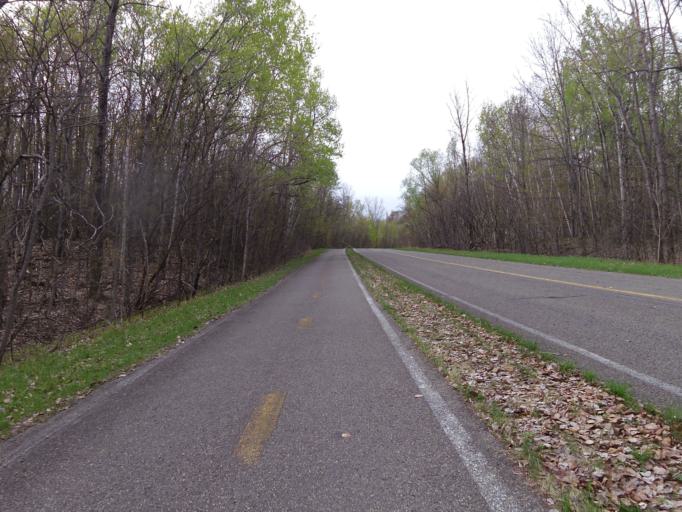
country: CA
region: Quebec
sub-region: Laurentides
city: Sainte-Marthe-sur-le-Lac
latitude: 45.4962
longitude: -74.0065
